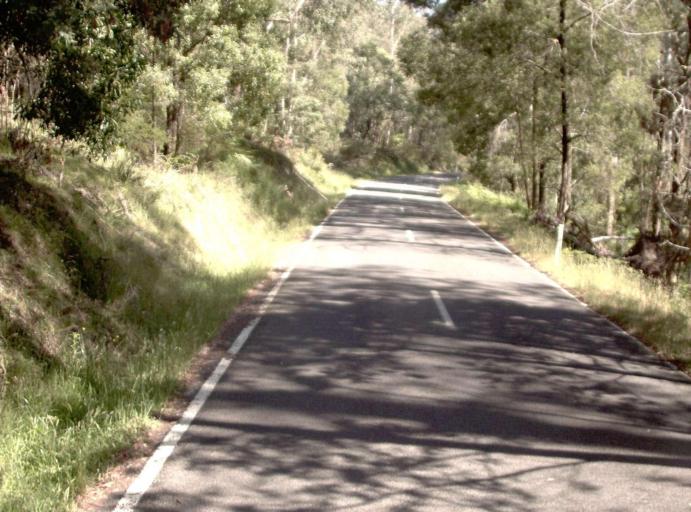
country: AU
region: New South Wales
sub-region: Bombala
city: Bombala
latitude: -37.3639
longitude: 148.6843
